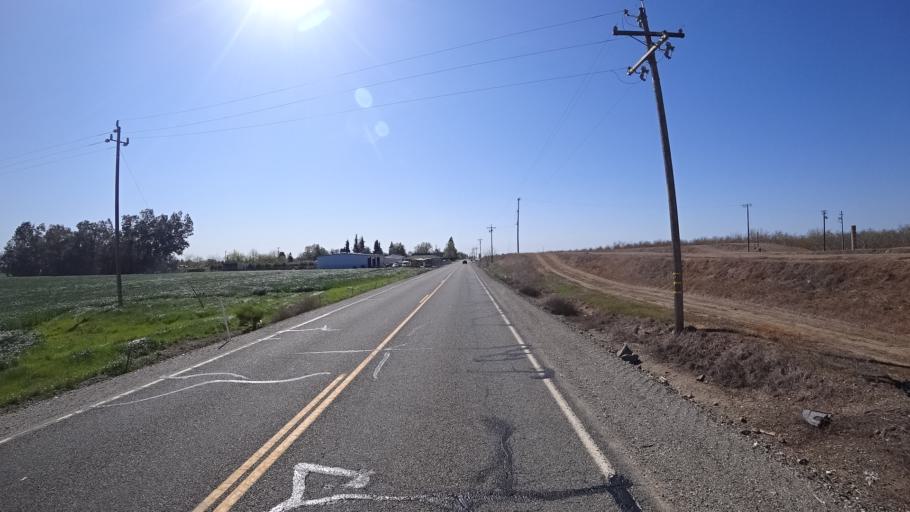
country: US
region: California
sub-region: Glenn County
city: Hamilton City
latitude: 39.7483
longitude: -122.0210
